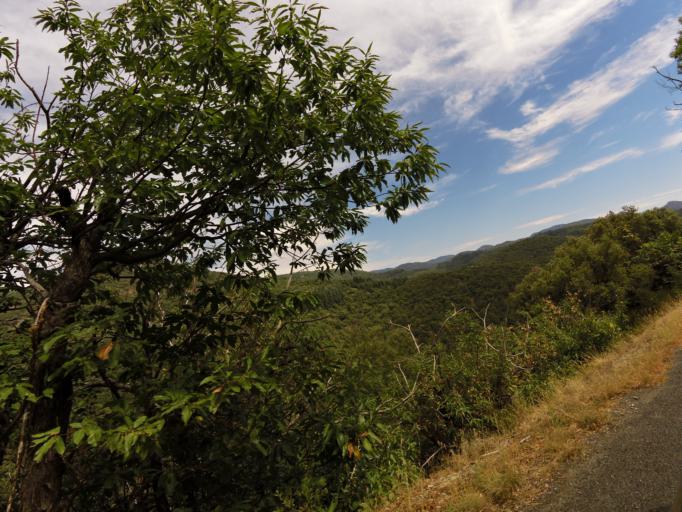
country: FR
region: Languedoc-Roussillon
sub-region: Departement du Gard
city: Le Vigan
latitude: 44.0150
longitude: 3.6426
